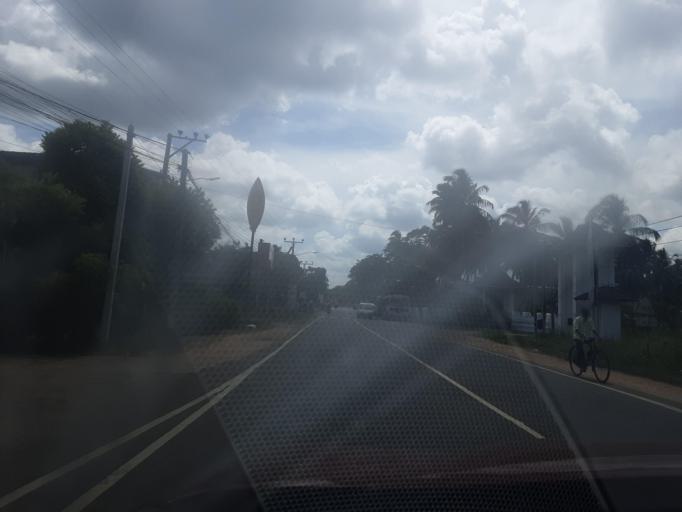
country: LK
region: North Western
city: Kuliyapitiya
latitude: 7.4703
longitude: 80.0464
